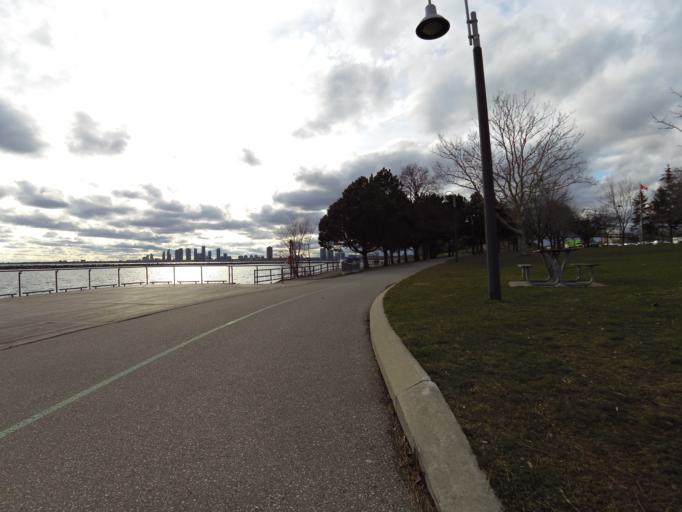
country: CA
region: Ontario
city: Toronto
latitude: 43.6309
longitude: -79.4334
